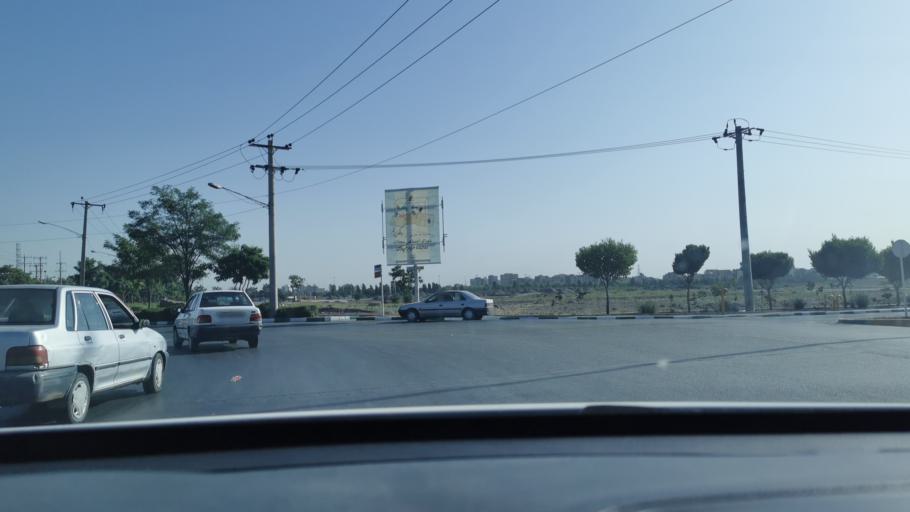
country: IR
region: Razavi Khorasan
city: Mashhad
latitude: 36.3410
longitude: 59.5080
